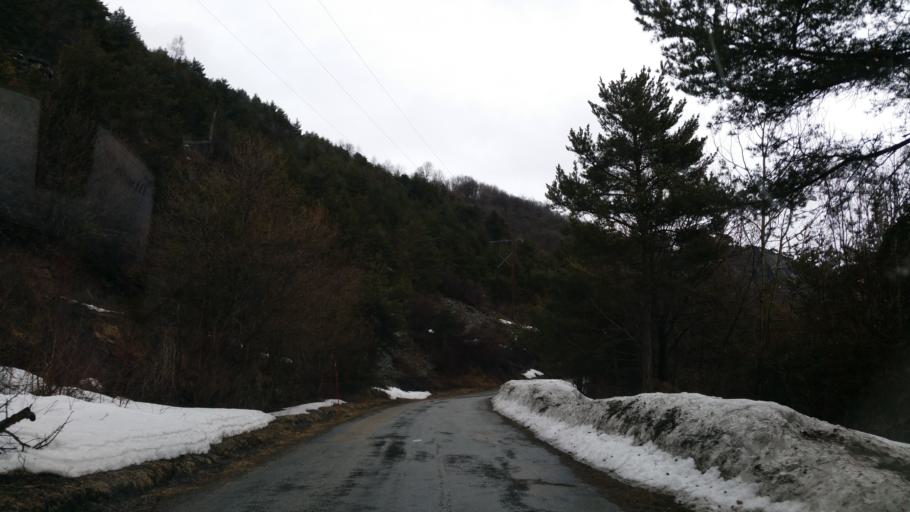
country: FR
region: Rhone-Alpes
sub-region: Departement de la Savoie
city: Villargondran
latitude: 45.2775
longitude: 6.3955
